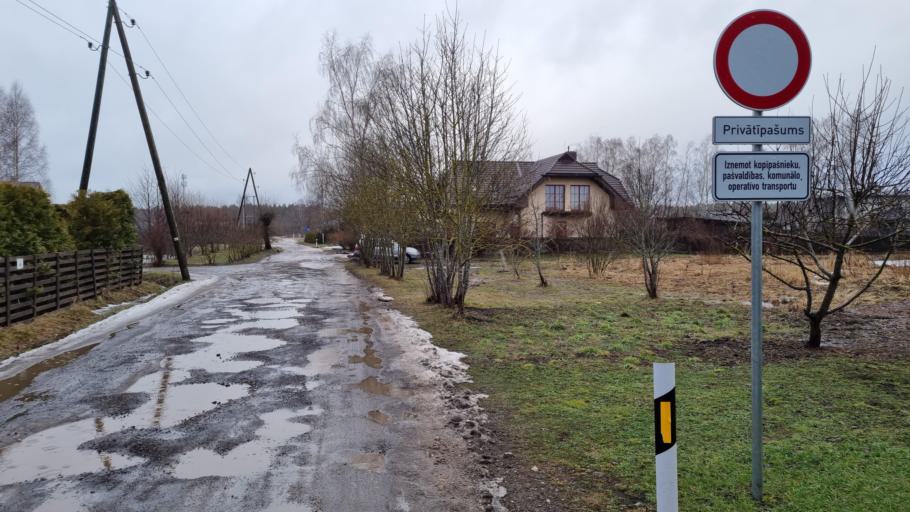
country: LV
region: Riga
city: Daugavgriva
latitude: 56.9864
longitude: 23.9952
